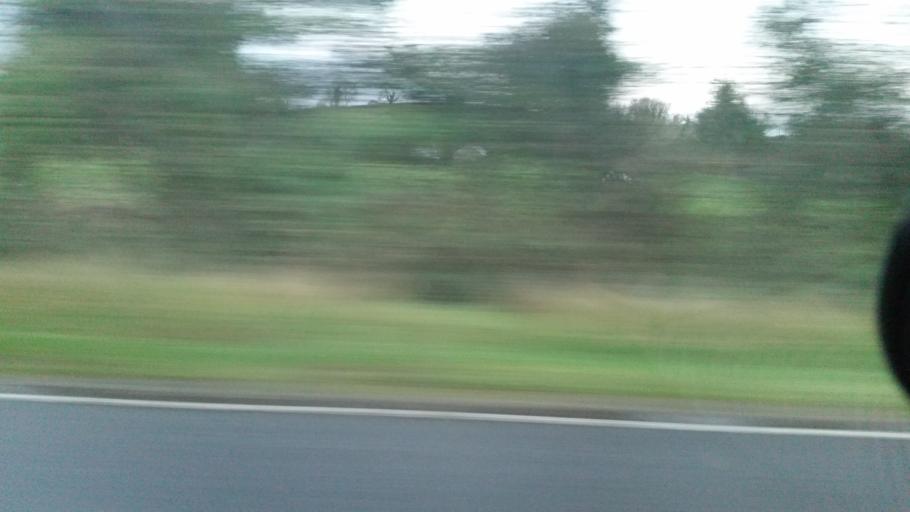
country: IE
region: Ulster
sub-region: County Monaghan
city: Monaghan
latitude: 54.4236
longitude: -6.9835
